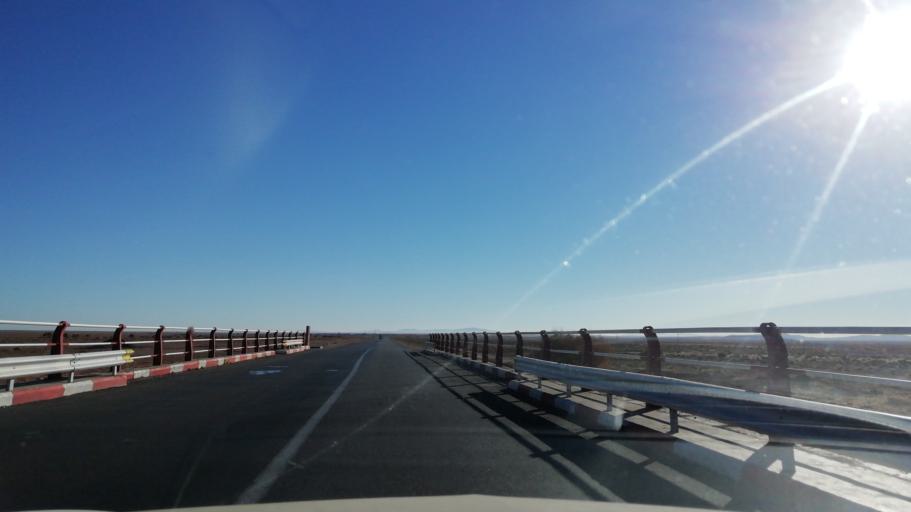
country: DZ
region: El Bayadh
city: El Bayadh
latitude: 33.8572
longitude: 0.5832
